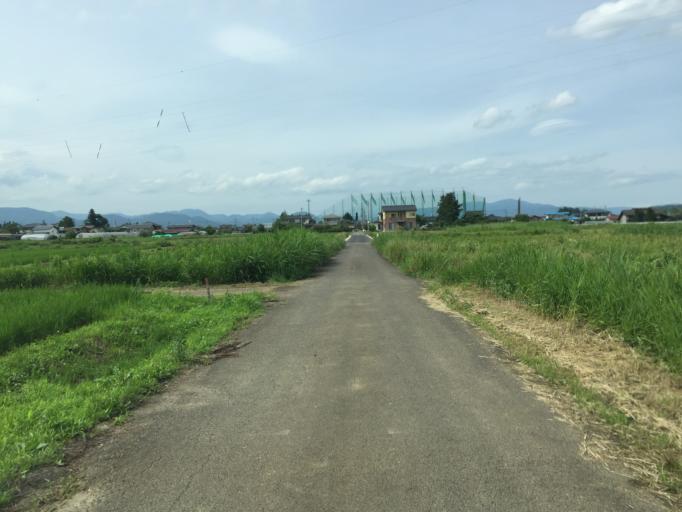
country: JP
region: Fukushima
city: Fukushima-shi
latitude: 37.7355
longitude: 140.4335
